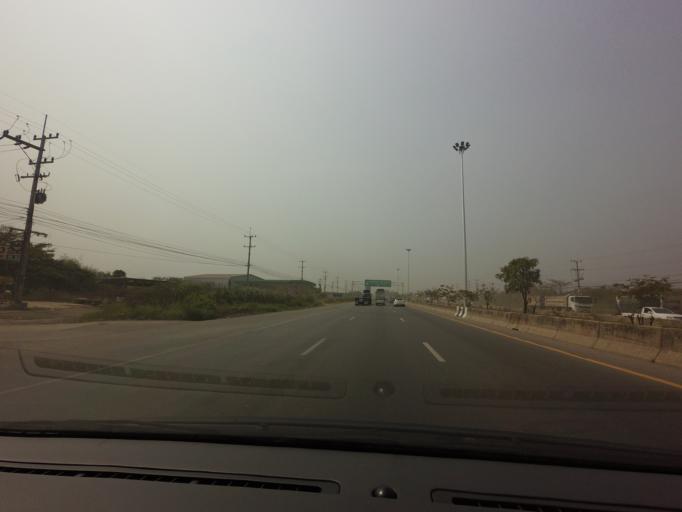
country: TH
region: Samut Songkhram
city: Samut Songkhram
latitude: 13.4522
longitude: 100.0837
